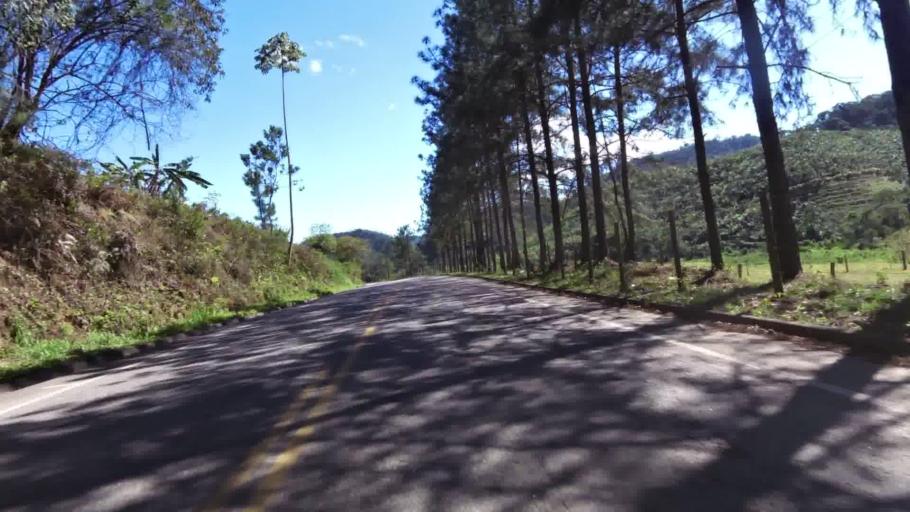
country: BR
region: Espirito Santo
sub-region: Vargem Alta
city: Vargem Alta
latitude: -20.6714
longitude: -40.9569
